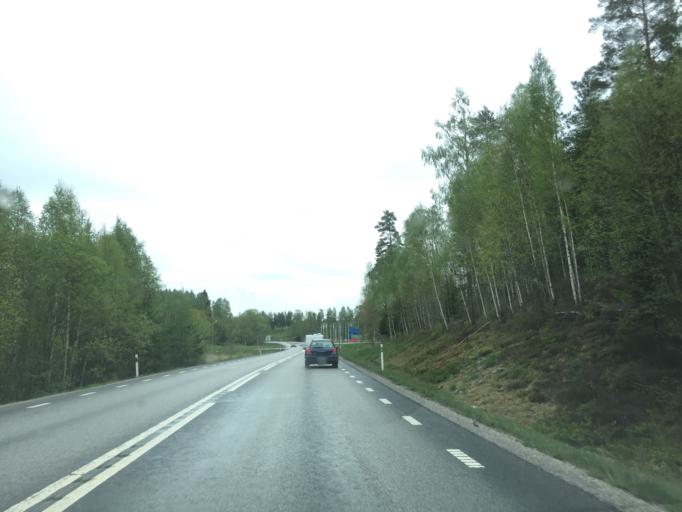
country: SE
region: OErebro
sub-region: Lindesbergs Kommun
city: Lindesberg
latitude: 59.5993
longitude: 15.1842
